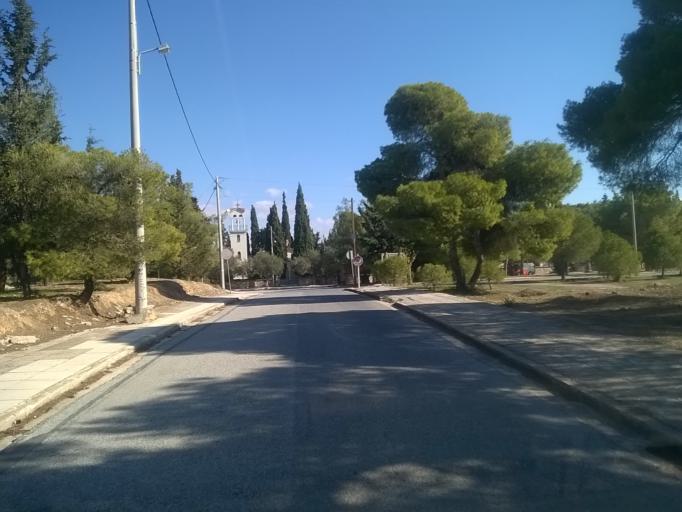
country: GR
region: Attica
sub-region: Nomarchia Anatolikis Attikis
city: Vouliagmeni
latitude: 37.8148
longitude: 23.7896
